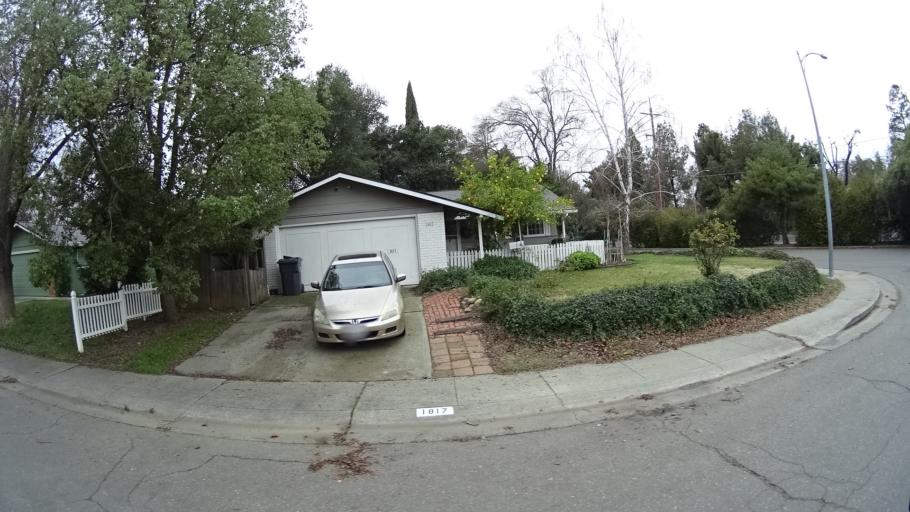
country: US
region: California
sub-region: Yolo County
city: Davis
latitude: 38.5624
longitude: -121.7252
